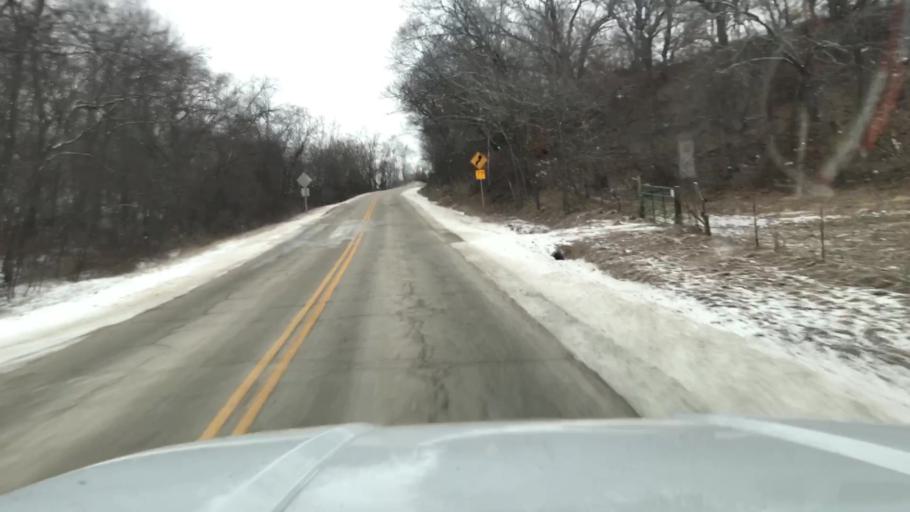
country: US
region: Missouri
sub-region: Andrew County
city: Savannah
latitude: 40.0237
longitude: -94.9166
